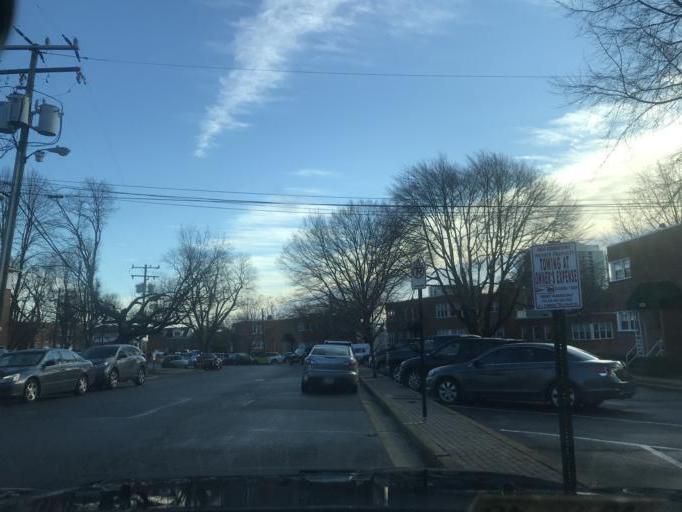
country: US
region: Virginia
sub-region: Arlington County
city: Arlington
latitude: 38.8986
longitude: -77.0794
